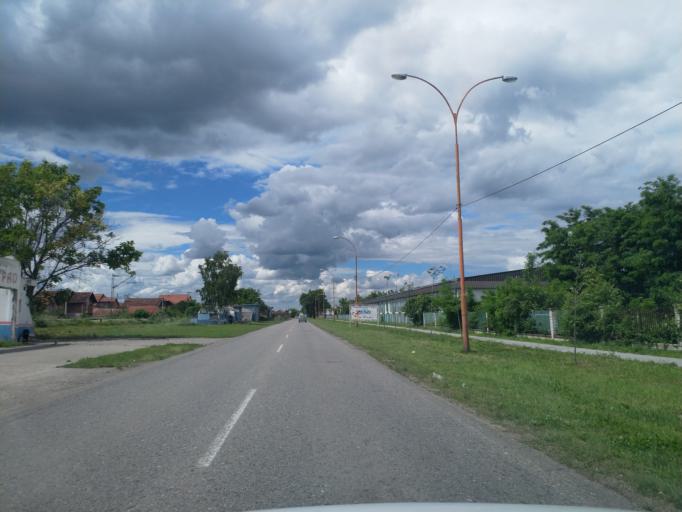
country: RS
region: Central Serbia
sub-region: Pomoravski Okrug
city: Cuprija
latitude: 43.9065
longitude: 21.3782
